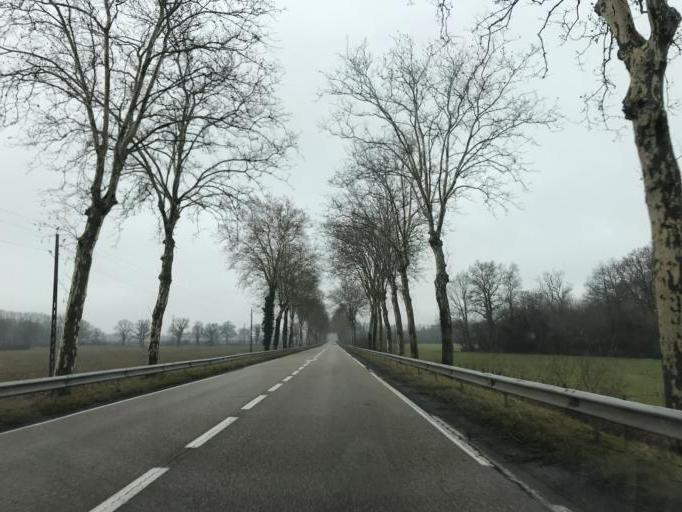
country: FR
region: Rhone-Alpes
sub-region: Departement de l'Ain
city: Servas
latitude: 46.1262
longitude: 5.1599
